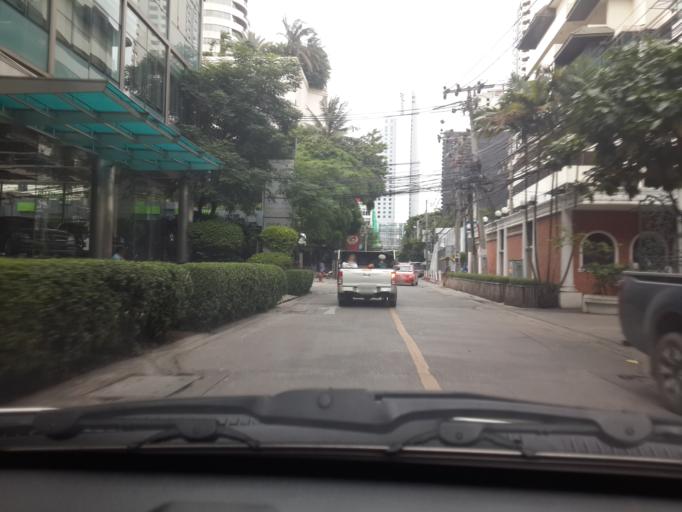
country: TH
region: Bangkok
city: Khlong Toei
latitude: 13.7309
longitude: 100.5638
